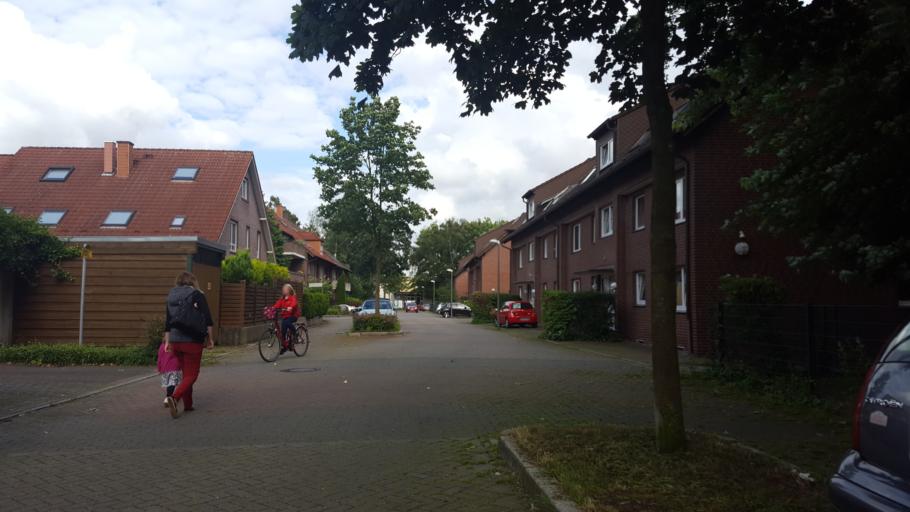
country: DE
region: North Rhine-Westphalia
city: Oer-Erkenschwick
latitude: 51.6384
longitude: 7.2704
